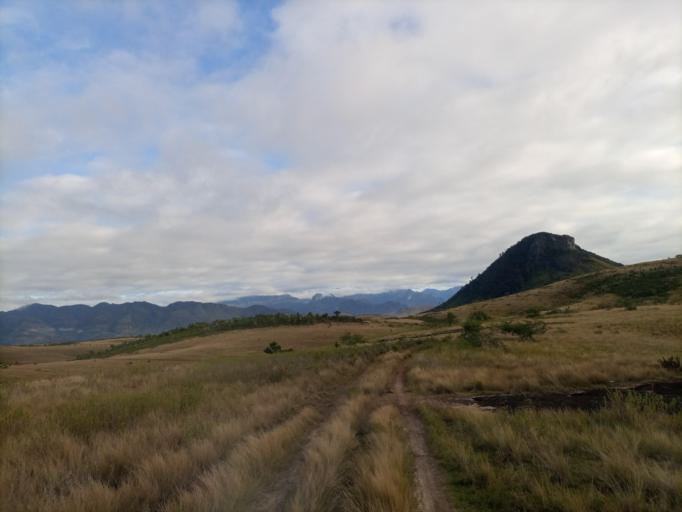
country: MG
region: Anosy
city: Fort Dauphin
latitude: -24.3137
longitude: 47.2622
